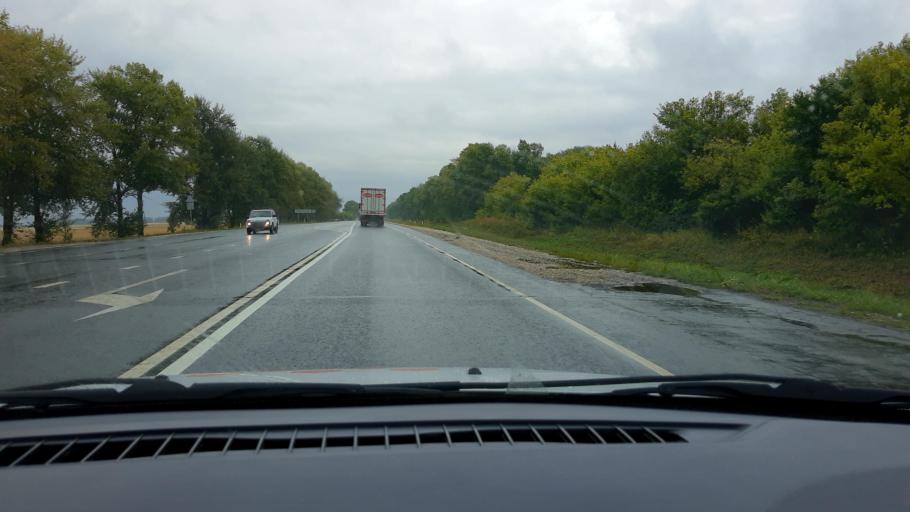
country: RU
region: Chuvashia
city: Yantikovo
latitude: 55.7897
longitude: 47.6969
